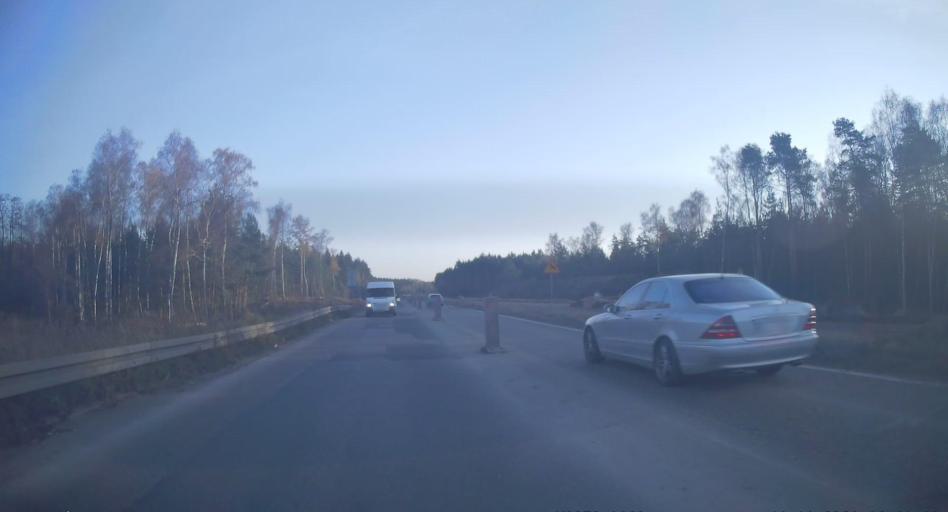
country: PL
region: Silesian Voivodeship
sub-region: Dabrowa Gornicza
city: Dabrowa Gornicza
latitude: 50.3739
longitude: 19.2458
